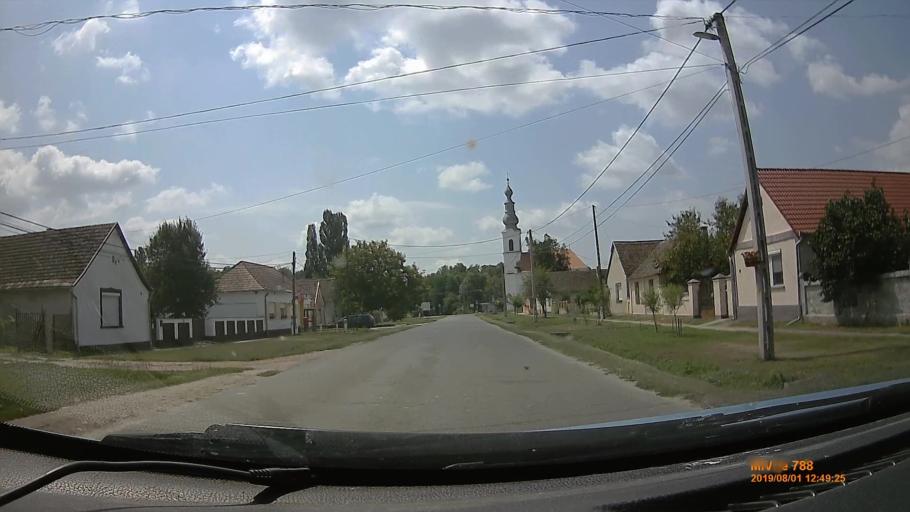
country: HR
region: Osjecko-Baranjska
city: Viljevo
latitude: 45.8147
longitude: 18.1053
